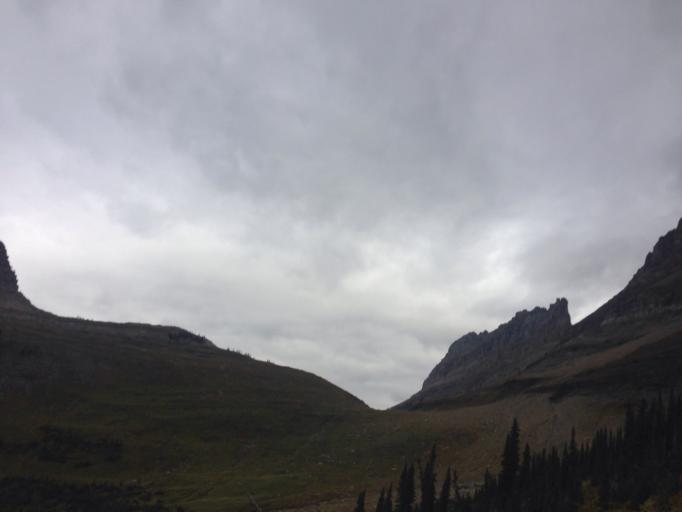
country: US
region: Montana
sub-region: Flathead County
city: Columbia Falls
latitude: 48.7308
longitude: -113.7198
